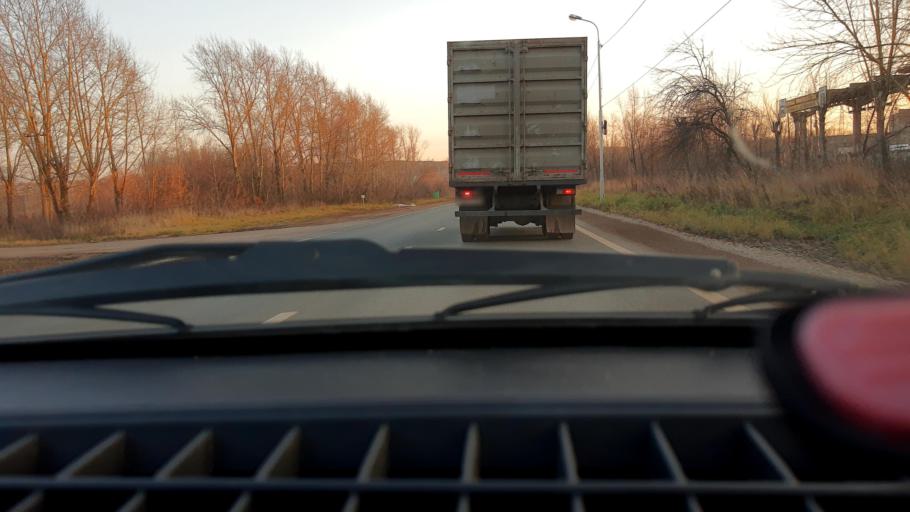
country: RU
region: Bashkortostan
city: Ufa
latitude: 54.8442
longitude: 56.1212
